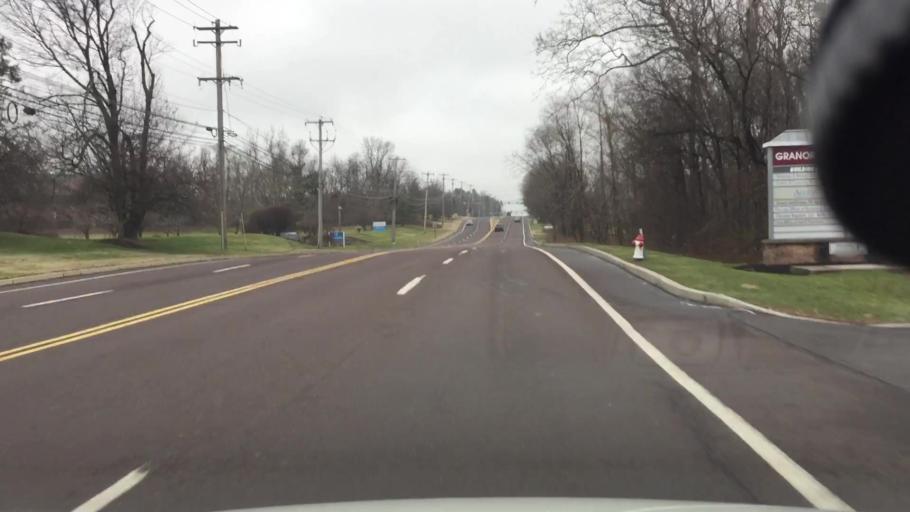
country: US
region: Pennsylvania
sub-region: Montgomery County
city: Horsham
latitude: 40.1659
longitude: -75.1472
